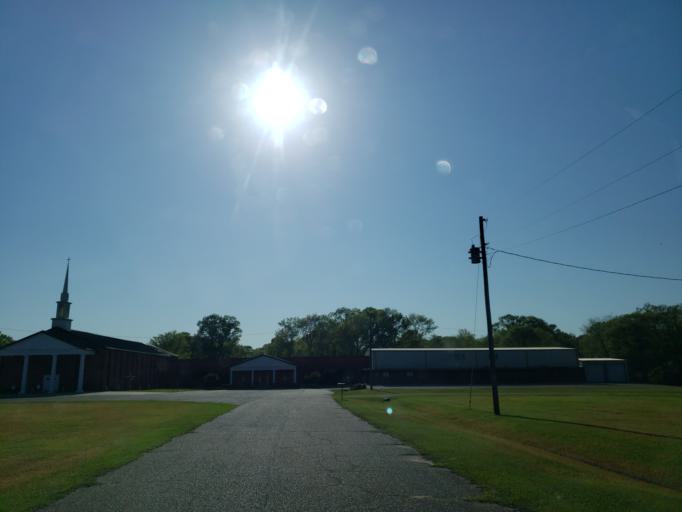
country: US
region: Mississippi
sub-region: Jones County
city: Ellisville
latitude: 31.6785
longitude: -89.3079
